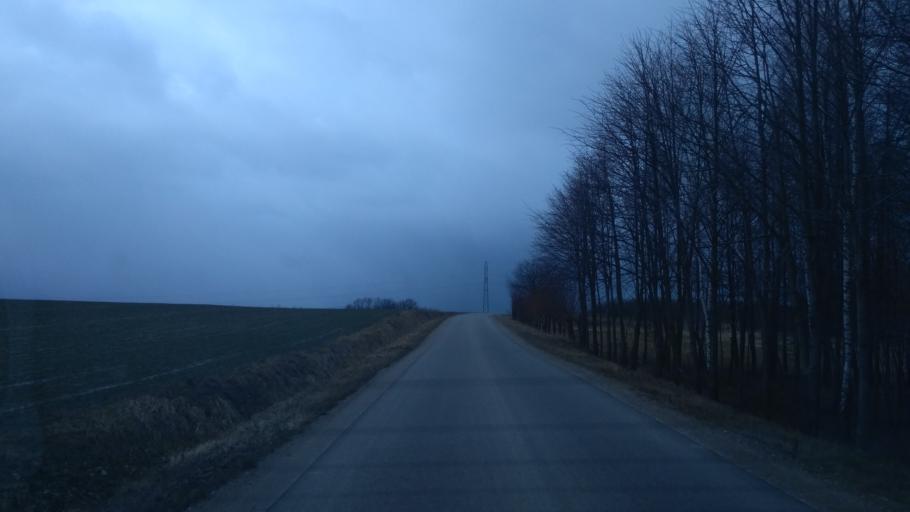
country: PL
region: Subcarpathian Voivodeship
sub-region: Powiat rzeszowski
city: Blazowa
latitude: 49.8886
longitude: 22.1268
